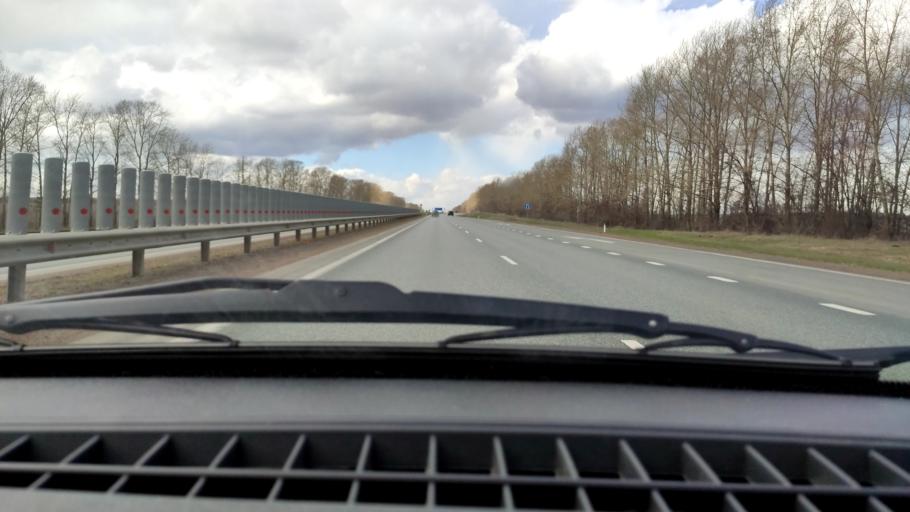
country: RU
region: Bashkortostan
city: Asanovo
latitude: 55.0262
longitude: 55.4681
